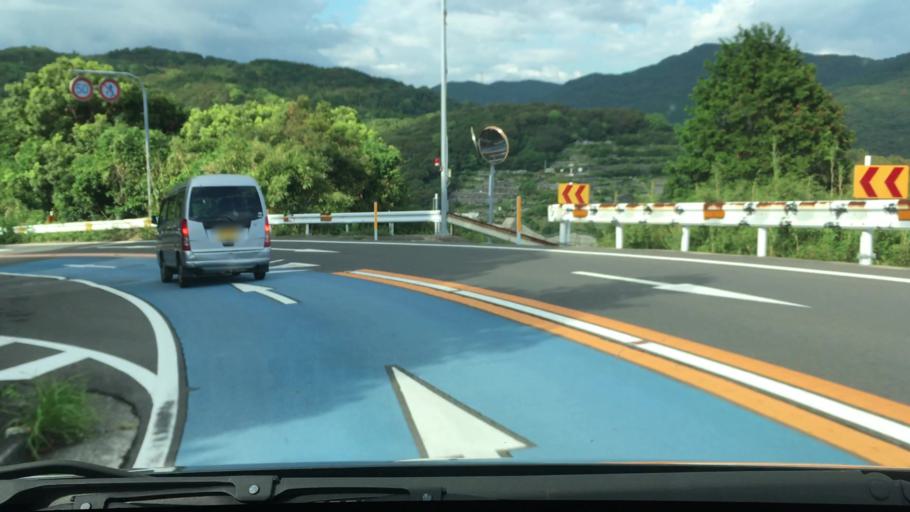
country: JP
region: Nagasaki
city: Togitsu
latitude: 32.8392
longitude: 129.7104
